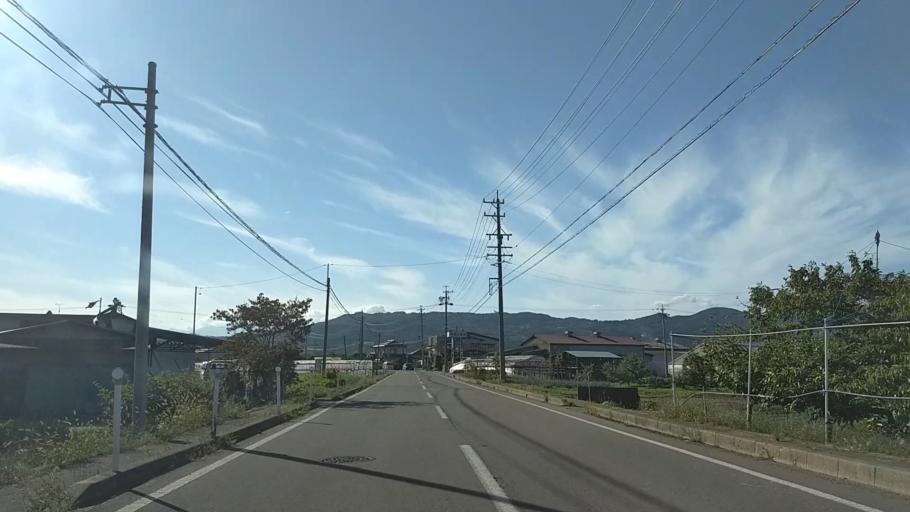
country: JP
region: Nagano
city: Nagano-shi
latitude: 36.5643
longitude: 138.1524
